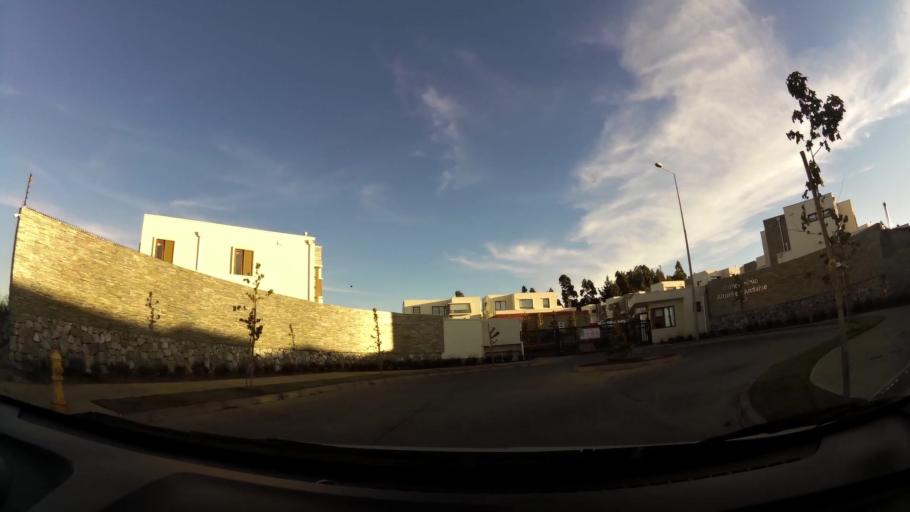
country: CL
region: Biobio
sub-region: Provincia de Concepcion
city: Concepcion
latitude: -36.8554
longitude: -73.0899
